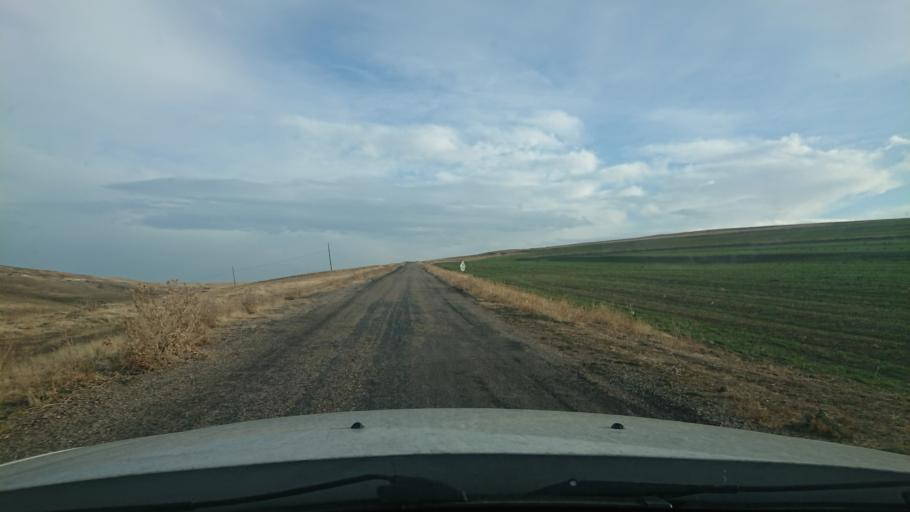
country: TR
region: Aksaray
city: Acipinar
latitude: 38.6550
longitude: 33.8343
